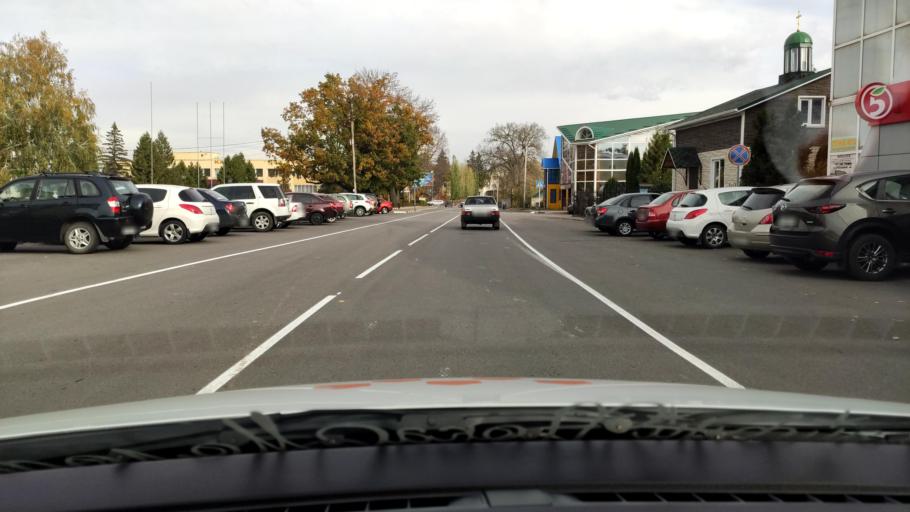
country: RU
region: Voronezj
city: Ramon'
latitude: 51.9118
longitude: 39.3385
